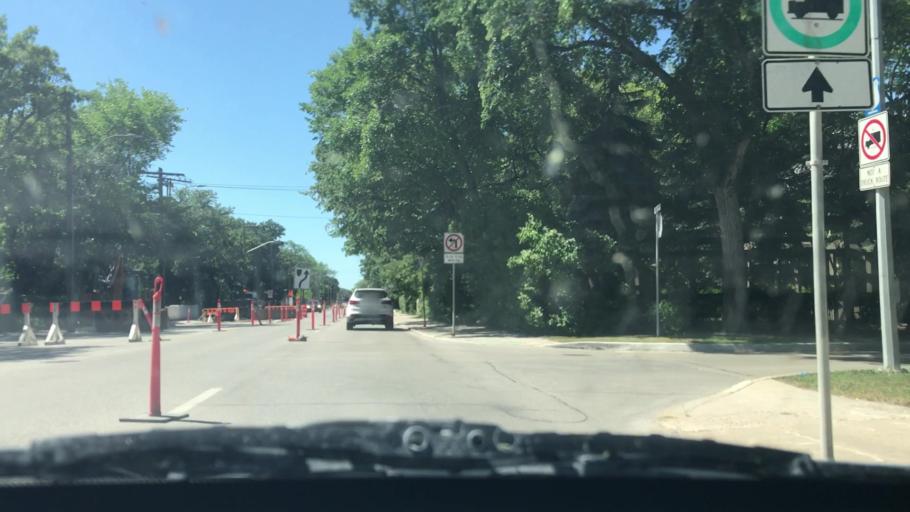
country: CA
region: Manitoba
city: Winnipeg
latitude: 49.8735
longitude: -97.1739
